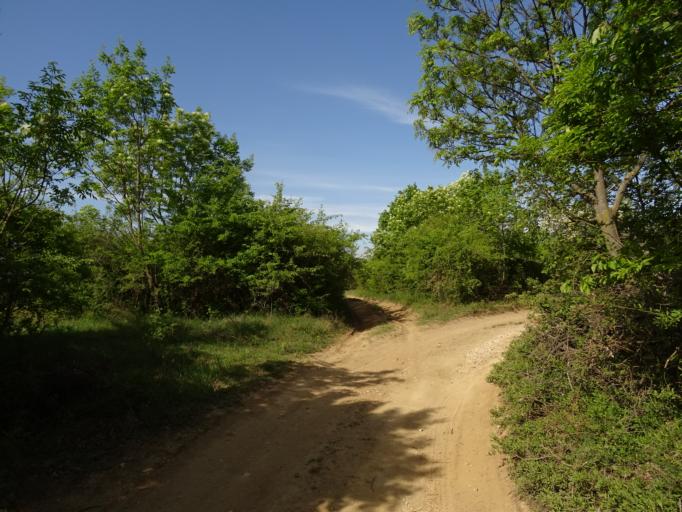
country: HU
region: Fejer
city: Szarliget
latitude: 47.4753
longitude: 18.4882
